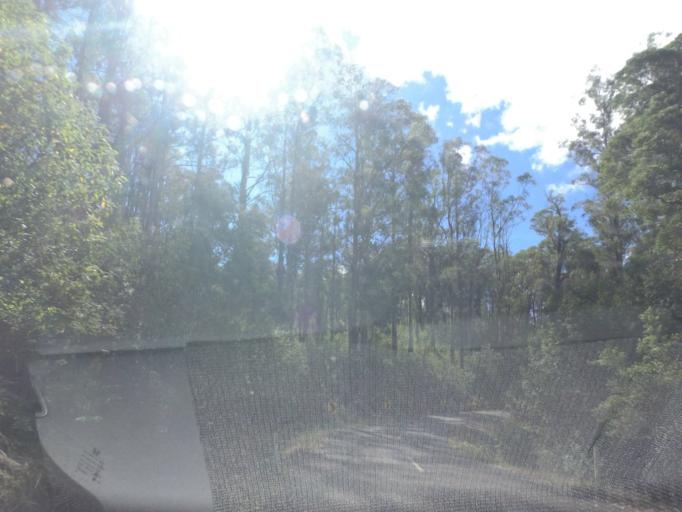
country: AU
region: Victoria
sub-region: Murrindindi
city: Alexandra
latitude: -37.3269
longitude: 145.9318
